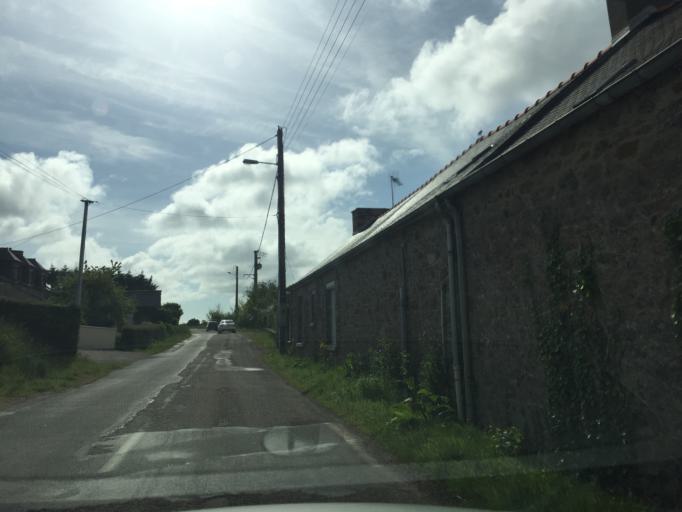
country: FR
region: Brittany
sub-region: Departement des Cotes-d'Armor
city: Matignon
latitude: 48.6238
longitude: -2.3428
